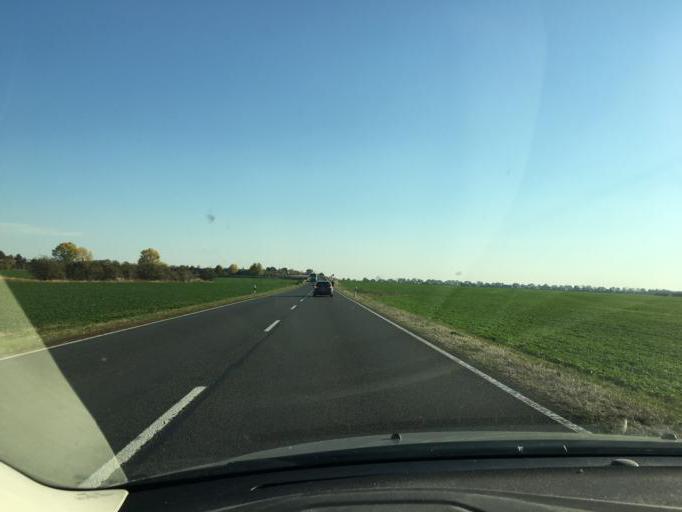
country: DE
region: Saxony
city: Rackwitz
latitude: 51.4277
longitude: 12.3719
